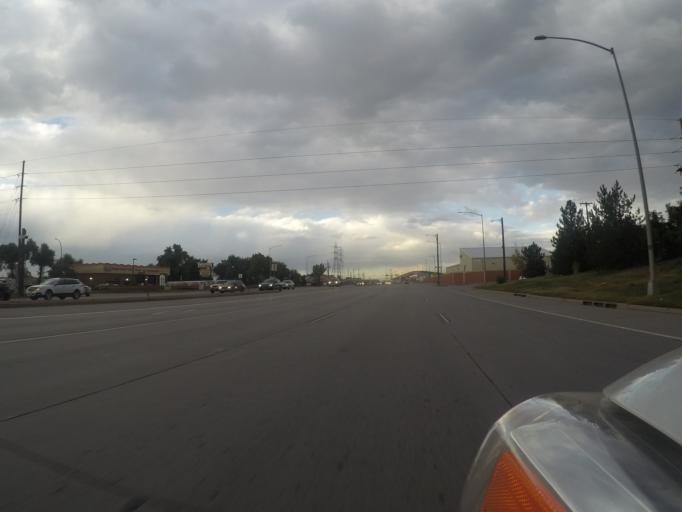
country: US
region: Colorado
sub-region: Arapahoe County
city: Littleton
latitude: 39.6272
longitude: -105.0111
